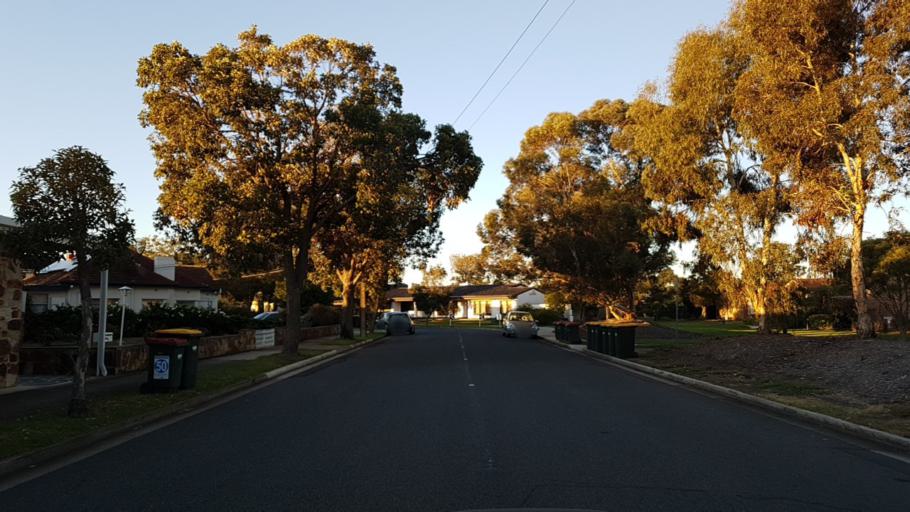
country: AU
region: South Australia
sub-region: Charles Sturt
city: Henley Beach
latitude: -34.9277
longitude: 138.5154
